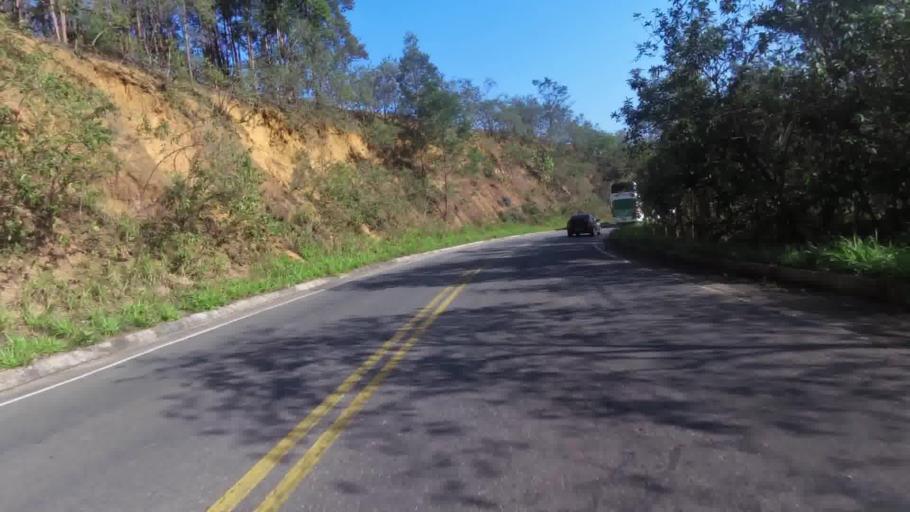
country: BR
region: Espirito Santo
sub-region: Alfredo Chaves
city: Alfredo Chaves
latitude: -20.6663
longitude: -40.7392
